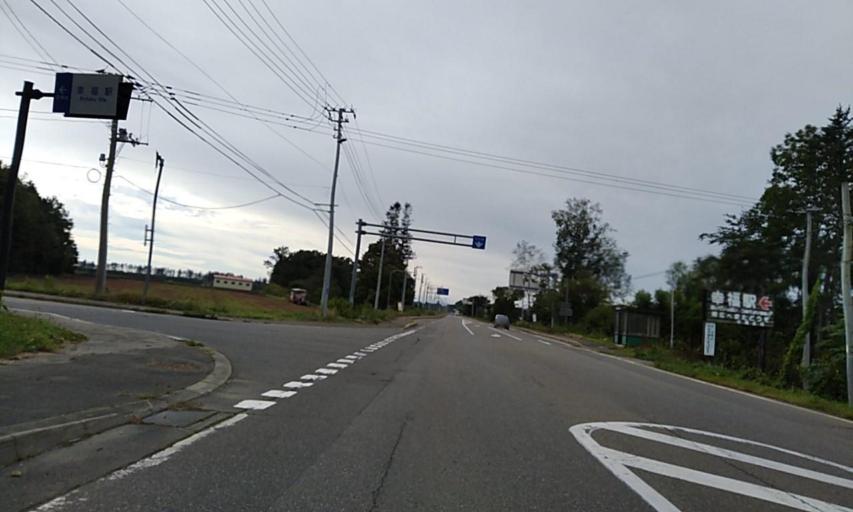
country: JP
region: Hokkaido
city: Obihiro
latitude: 42.7432
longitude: 143.1580
